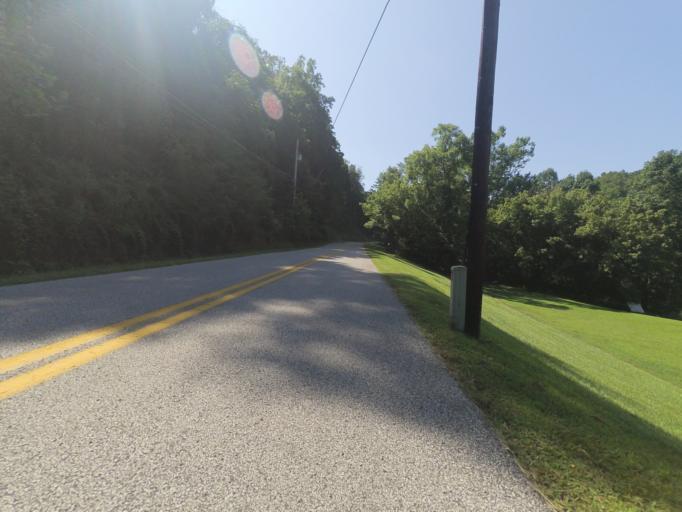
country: US
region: West Virginia
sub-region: Cabell County
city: Huntington
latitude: 38.3814
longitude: -82.4679
